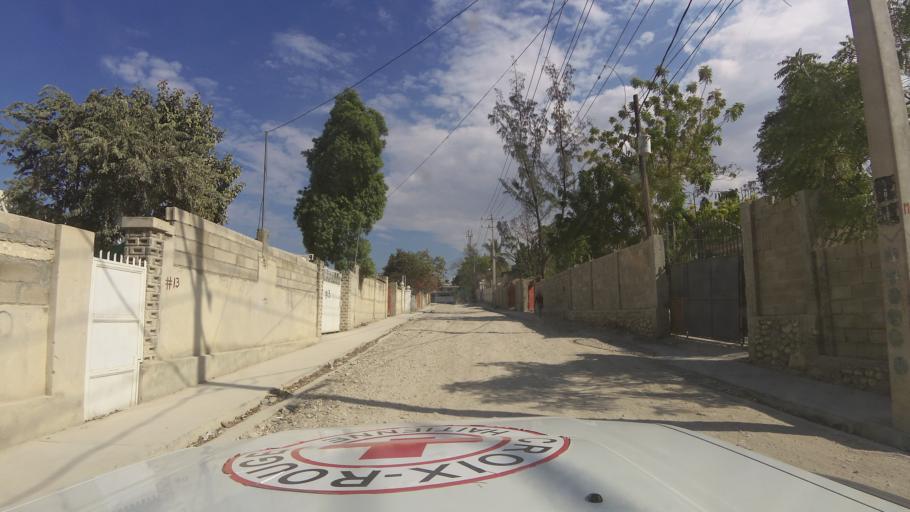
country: HT
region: Ouest
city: Delmas 73
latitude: 18.5606
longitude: -72.2989
